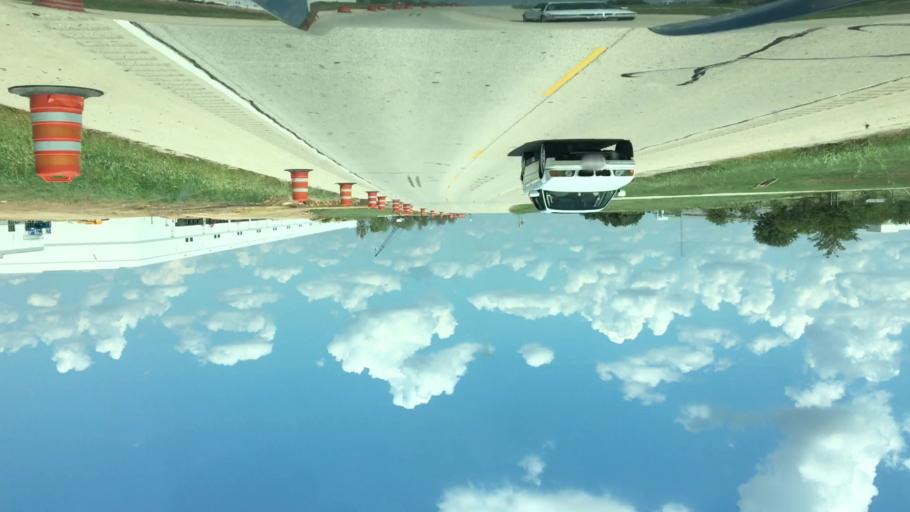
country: US
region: Texas
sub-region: Tarrant County
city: Haslet
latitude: 32.9832
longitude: -97.3419
